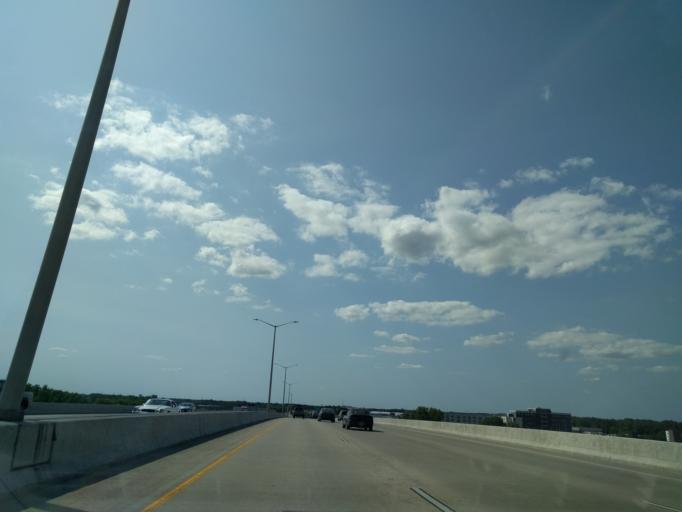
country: US
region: Wisconsin
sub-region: Brown County
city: Ashwaubenon
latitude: 44.4760
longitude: -88.0466
